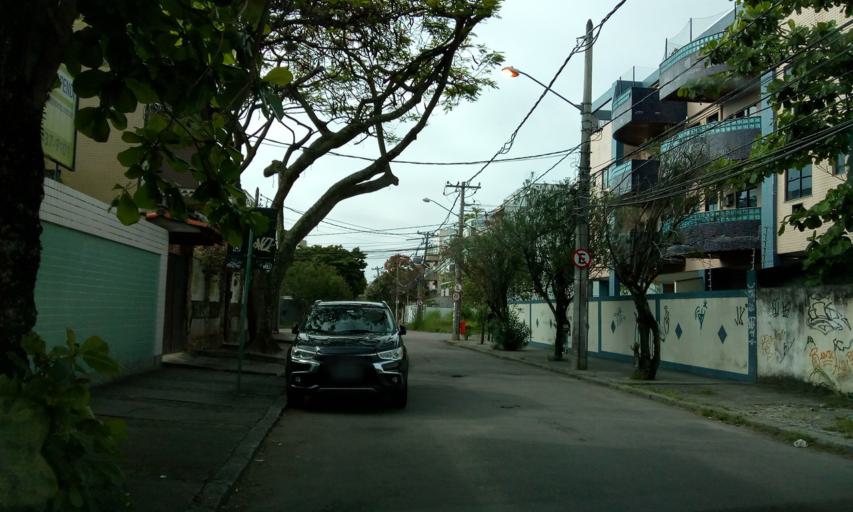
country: BR
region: Rio de Janeiro
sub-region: Nilopolis
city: Nilopolis
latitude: -23.0130
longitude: -43.4533
